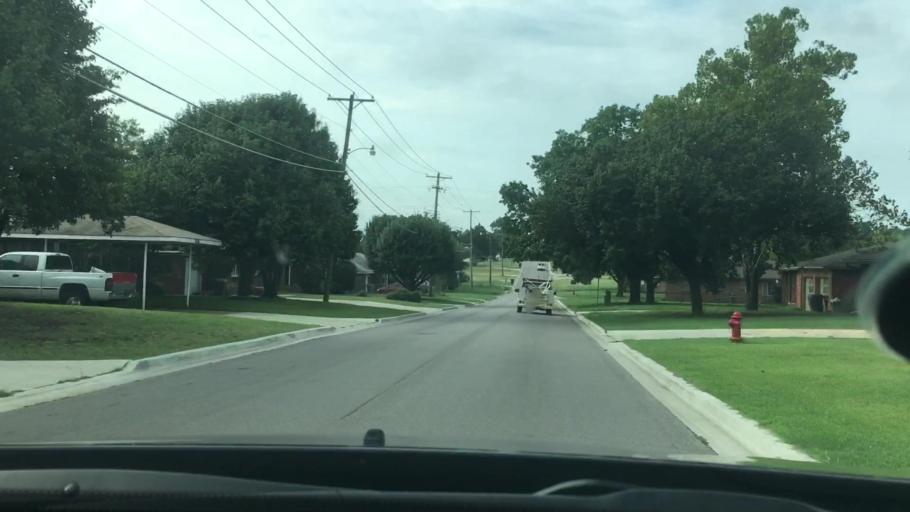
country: US
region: Oklahoma
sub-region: Carter County
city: Ardmore
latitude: 34.1926
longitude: -97.1255
